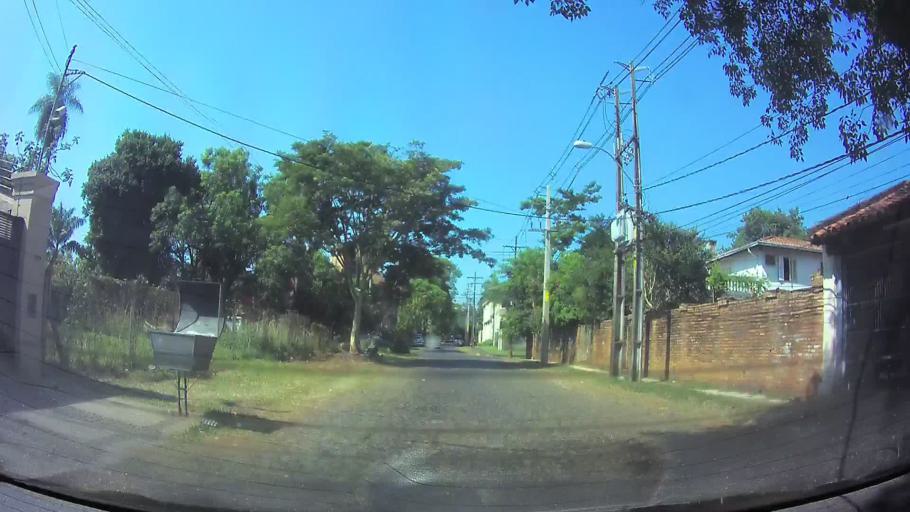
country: PY
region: Central
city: Fernando de la Mora
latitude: -25.2906
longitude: -57.5639
